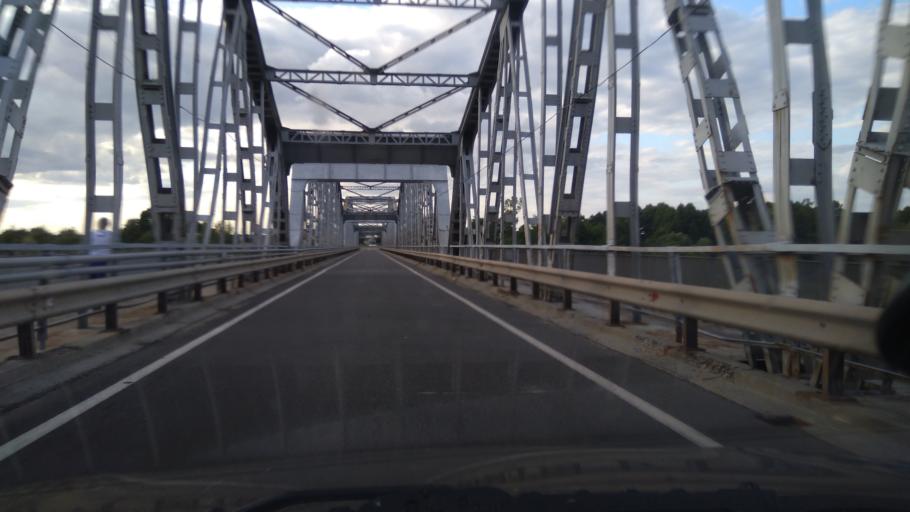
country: BY
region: Grodnenskaya
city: Masty
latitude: 53.4236
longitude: 24.6292
